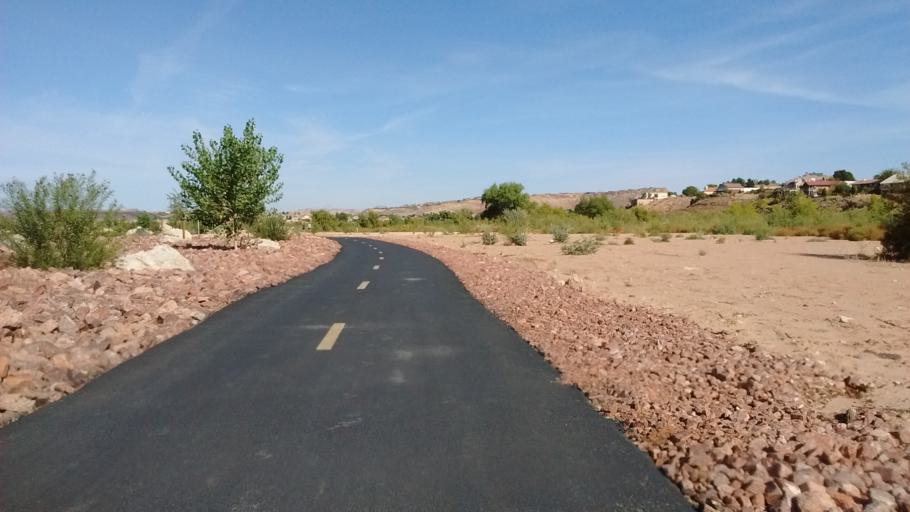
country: US
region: Utah
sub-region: Washington County
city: Saint George
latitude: 37.0751
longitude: -113.5807
